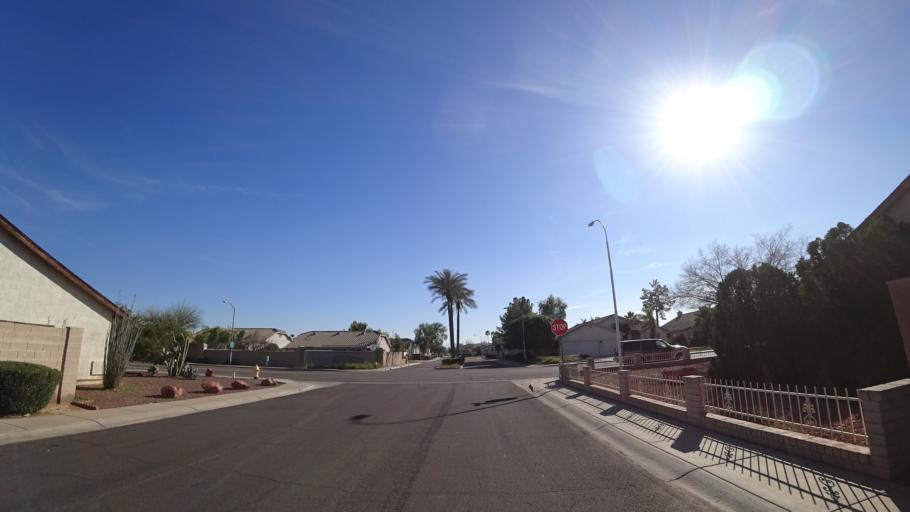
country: US
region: Arizona
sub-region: Maricopa County
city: Peoria
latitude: 33.5308
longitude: -112.2394
